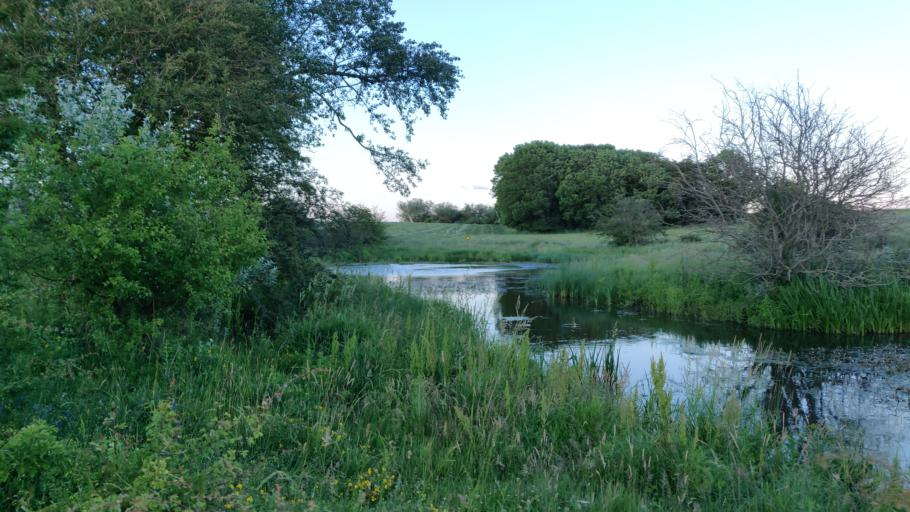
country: DK
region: Zealand
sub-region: Roskilde Kommune
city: Roskilde
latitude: 55.6857
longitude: 12.0764
